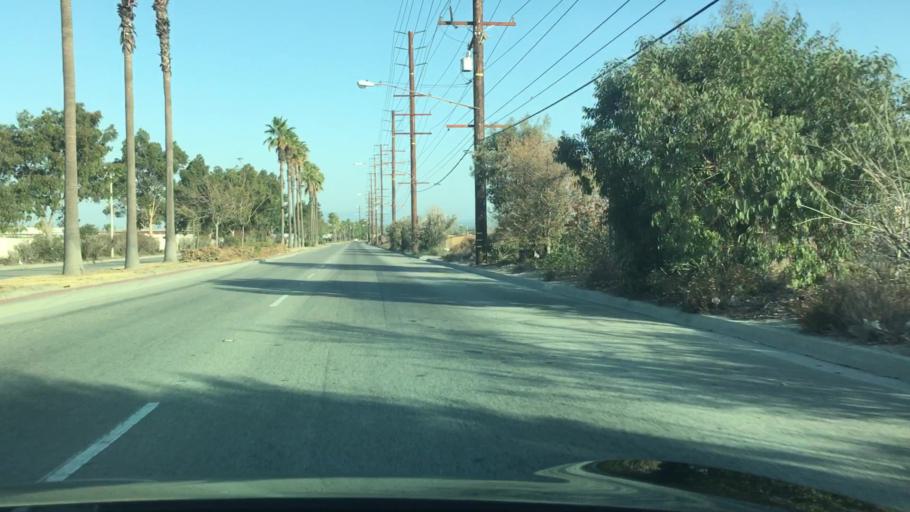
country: US
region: California
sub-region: Los Angeles County
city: Mayflower Village
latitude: 34.1109
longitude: -117.9858
